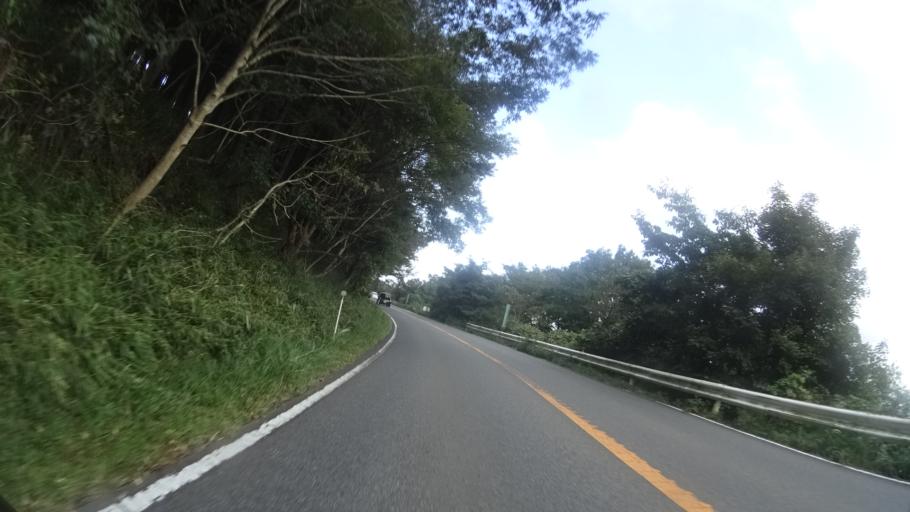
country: JP
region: Oita
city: Beppu
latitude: 33.2687
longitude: 131.4181
